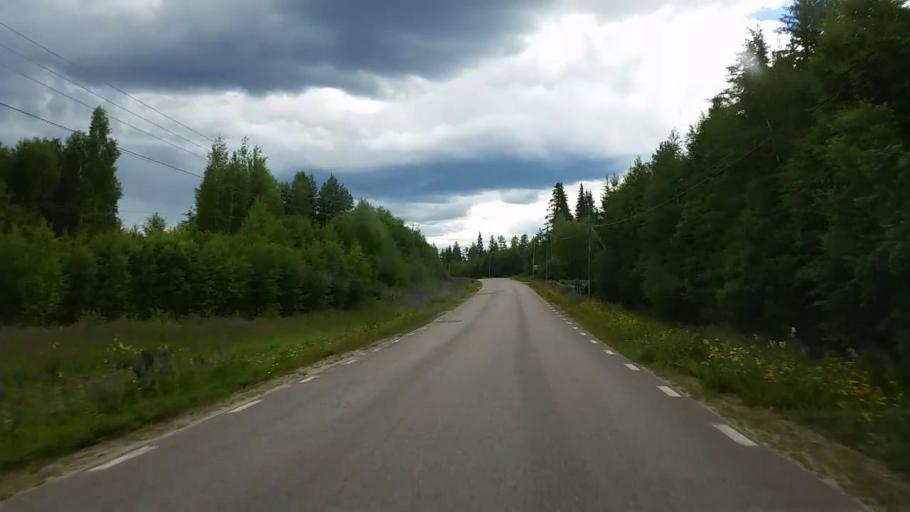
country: SE
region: Gaevleborg
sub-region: Ovanakers Kommun
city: Edsbyn
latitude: 61.4581
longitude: 15.8757
